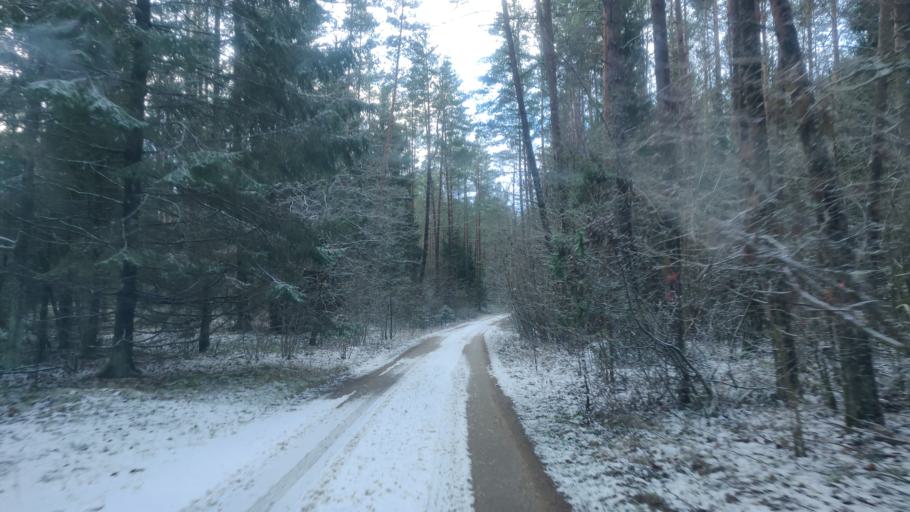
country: LT
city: Trakai
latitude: 54.5653
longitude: 24.9186
